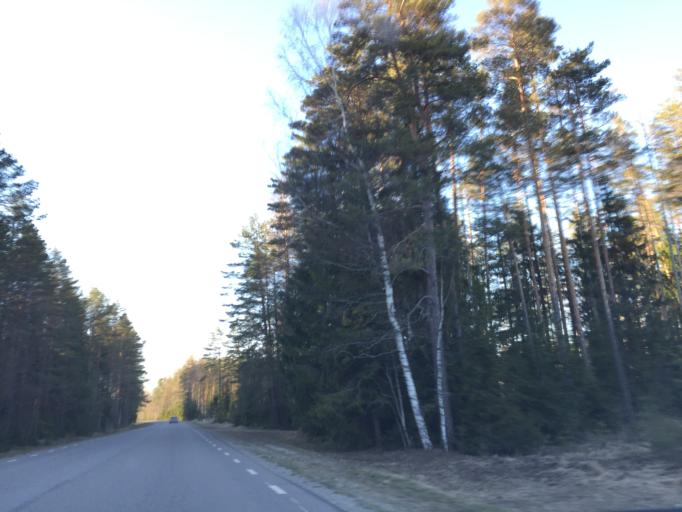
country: EE
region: Ida-Virumaa
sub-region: Toila vald
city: Voka
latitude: 59.1428
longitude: 27.6116
